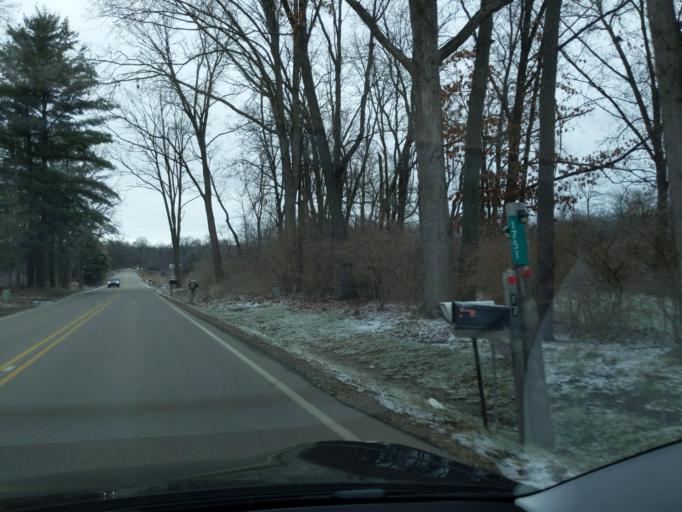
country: US
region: Michigan
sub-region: Jackson County
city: Spring Arbor
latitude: 42.2363
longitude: -84.5173
